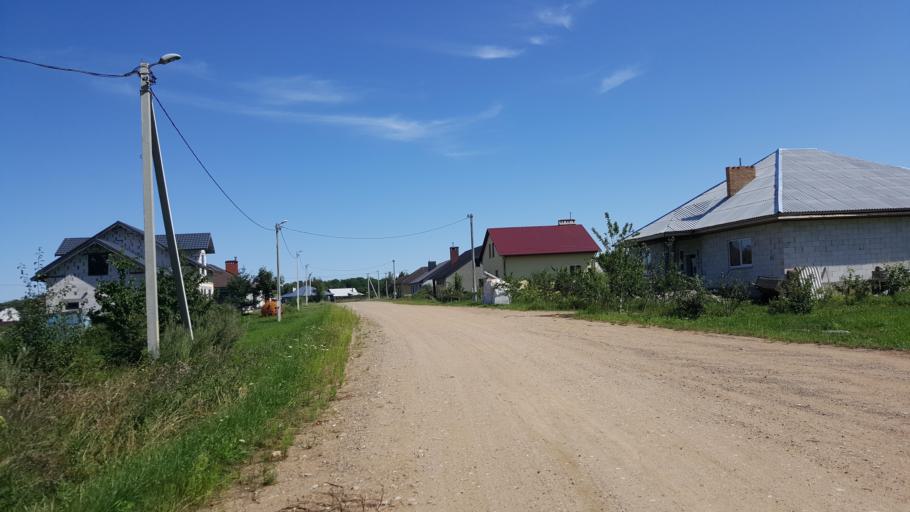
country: BY
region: Brest
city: Charnawchytsy
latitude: 52.2670
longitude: 23.7644
